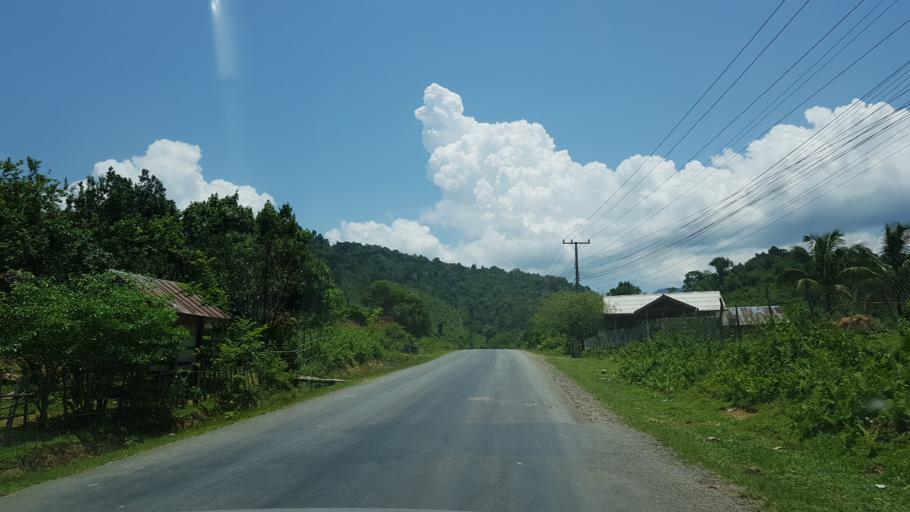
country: LA
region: Vientiane
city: Muang Kasi
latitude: 19.1316
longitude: 102.2277
